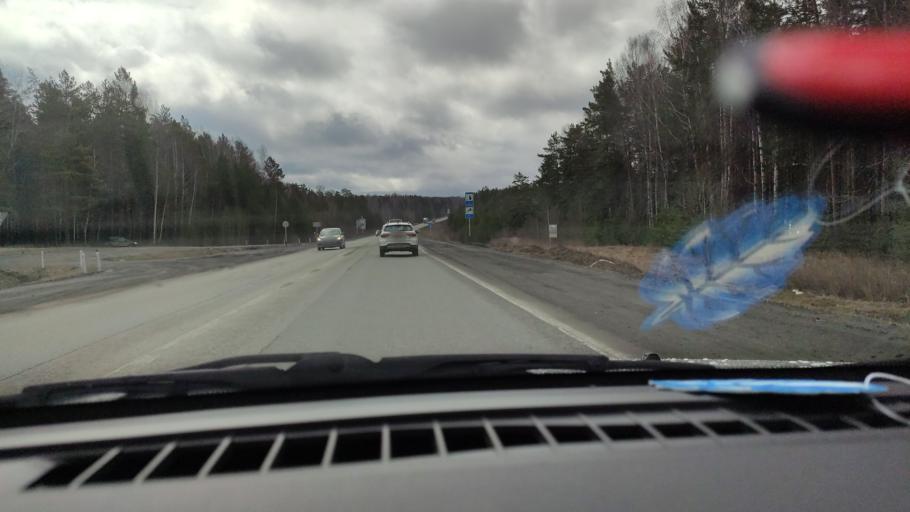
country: RU
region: Sverdlovsk
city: Talitsa
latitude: 56.8650
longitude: 60.0480
